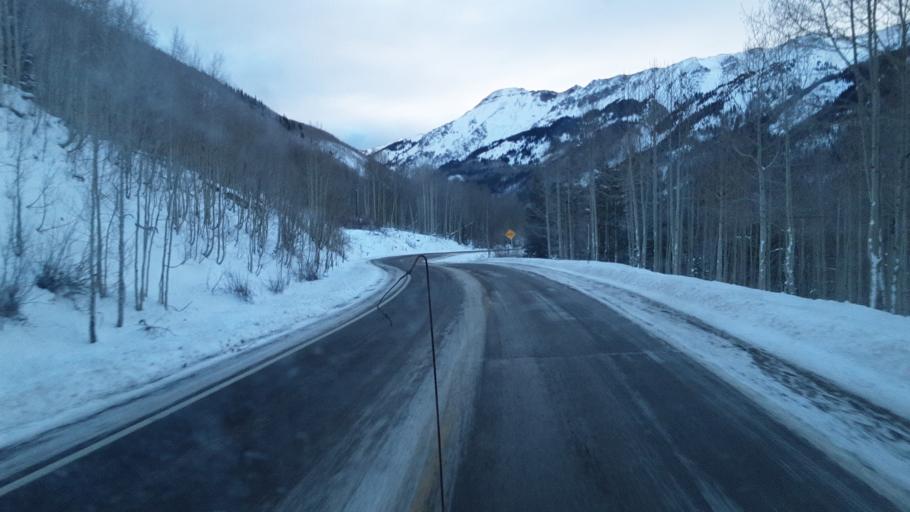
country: US
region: Colorado
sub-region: Ouray County
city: Ouray
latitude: 37.9304
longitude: -107.6869
